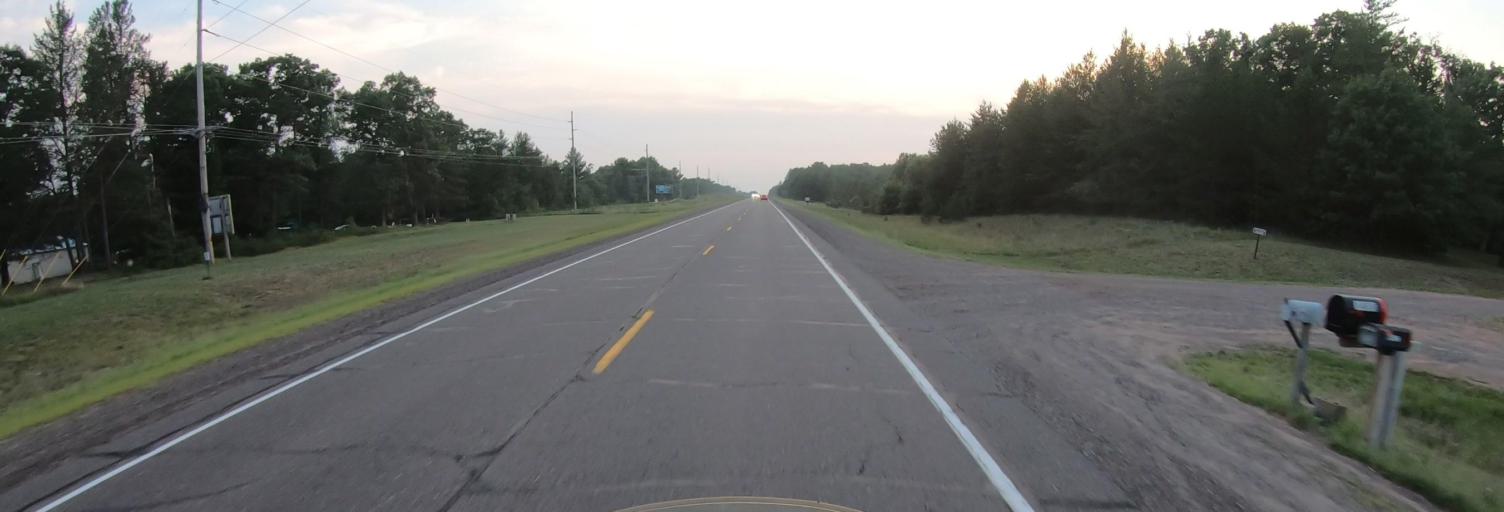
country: US
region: Wisconsin
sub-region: Burnett County
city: Grantsburg
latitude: 45.7732
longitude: -92.7358
